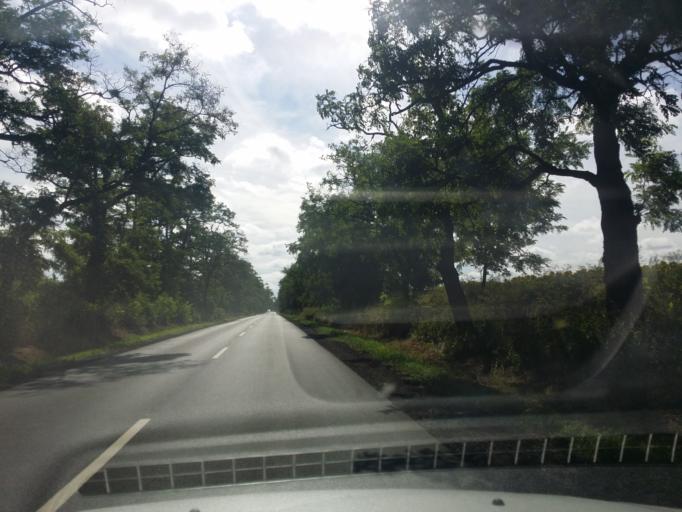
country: HU
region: Heves
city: Heves
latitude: 47.6229
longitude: 20.2563
